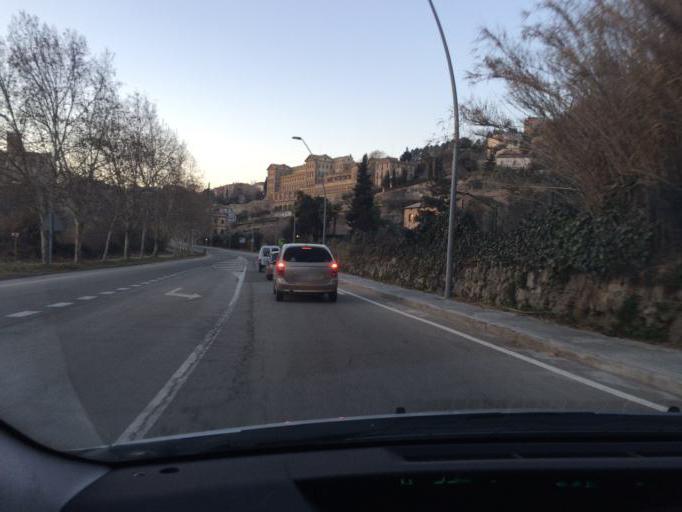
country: ES
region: Catalonia
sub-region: Provincia de Barcelona
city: Manresa
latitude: 41.7187
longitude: 1.8329
